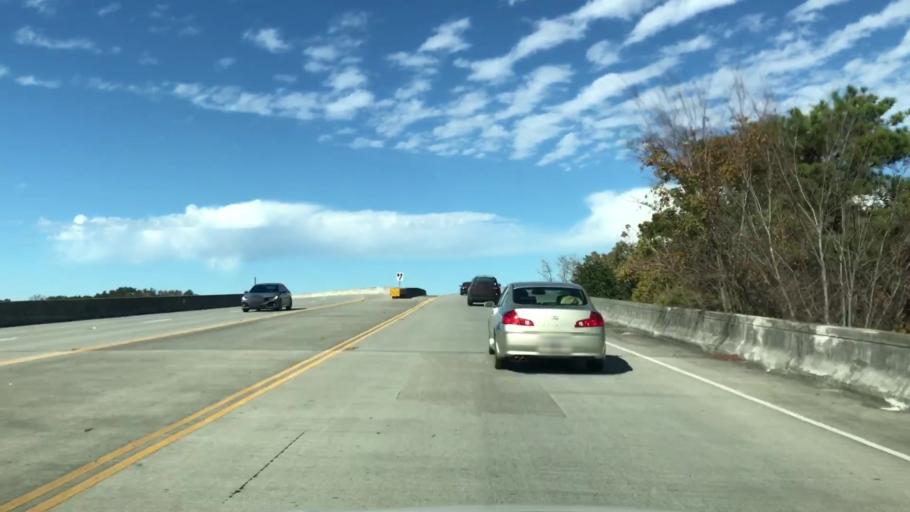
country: US
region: South Carolina
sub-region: Charleston County
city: Charleston
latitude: 32.7788
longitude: -79.9681
